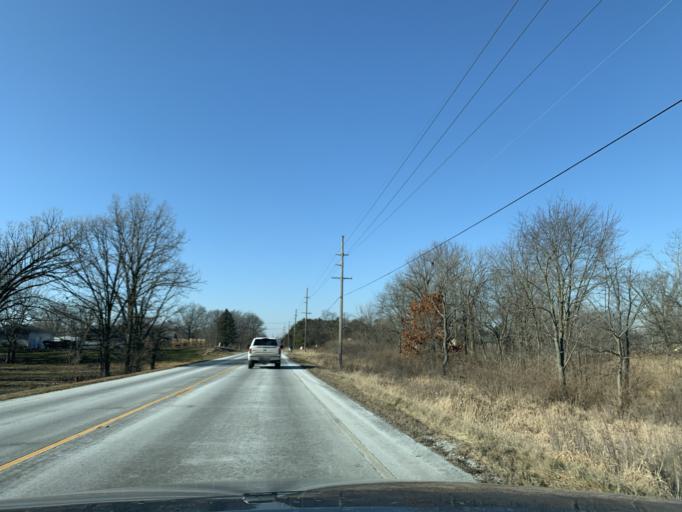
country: US
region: Indiana
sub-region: Lake County
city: Crown Point
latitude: 41.4208
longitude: -87.4111
